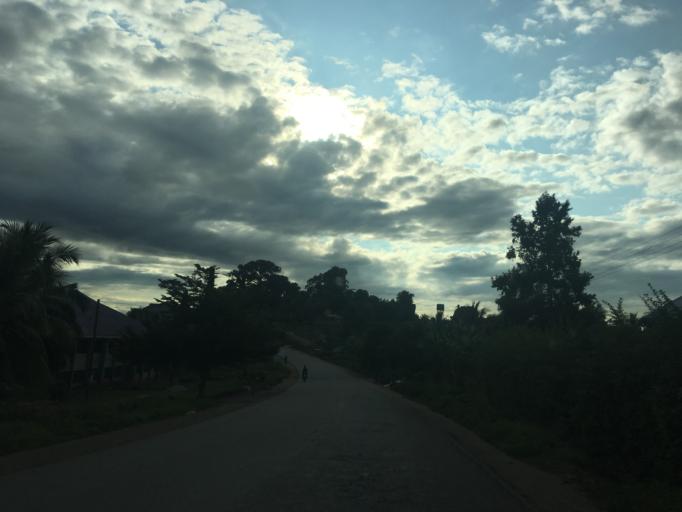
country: GH
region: Western
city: Bibiani
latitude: 6.3303
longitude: -2.2529
